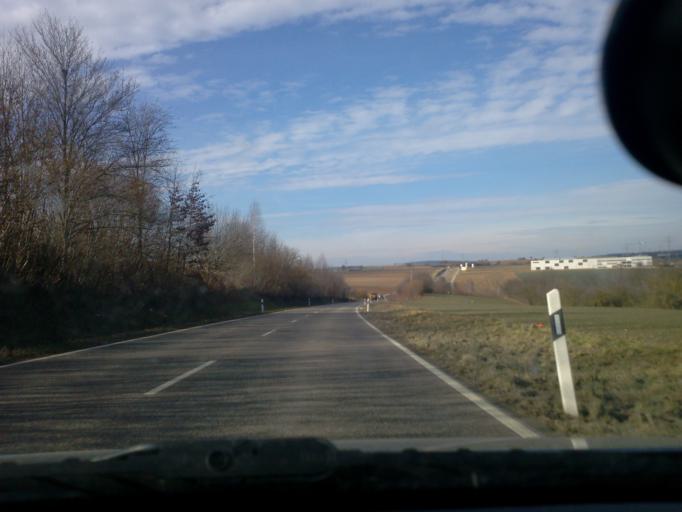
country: DE
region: Baden-Wuerttemberg
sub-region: Regierungsbezirk Stuttgart
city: Eppingen
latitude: 49.1405
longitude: 8.9321
